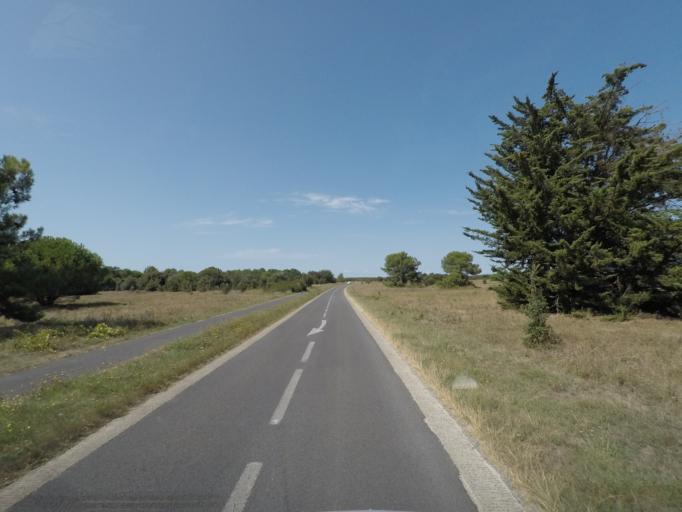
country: FR
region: Poitou-Charentes
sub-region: Departement de la Charente-Maritime
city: Sainte-Marie-de-Re
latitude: 46.1570
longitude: -1.3158
